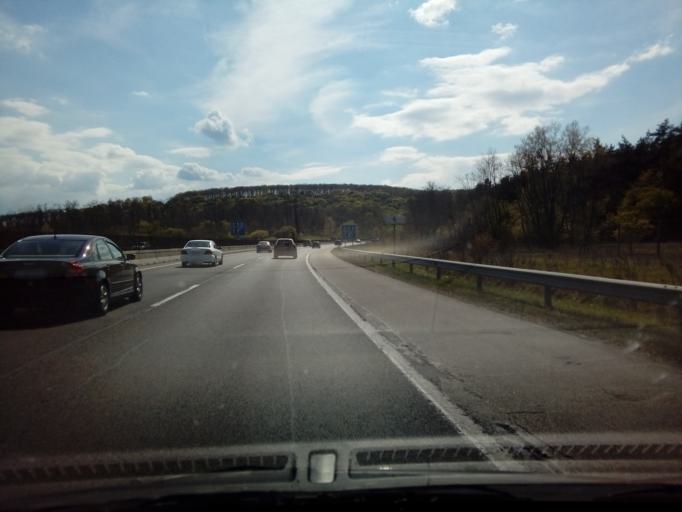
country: HU
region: Pest
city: Domony
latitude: 47.6163
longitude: 19.4053
